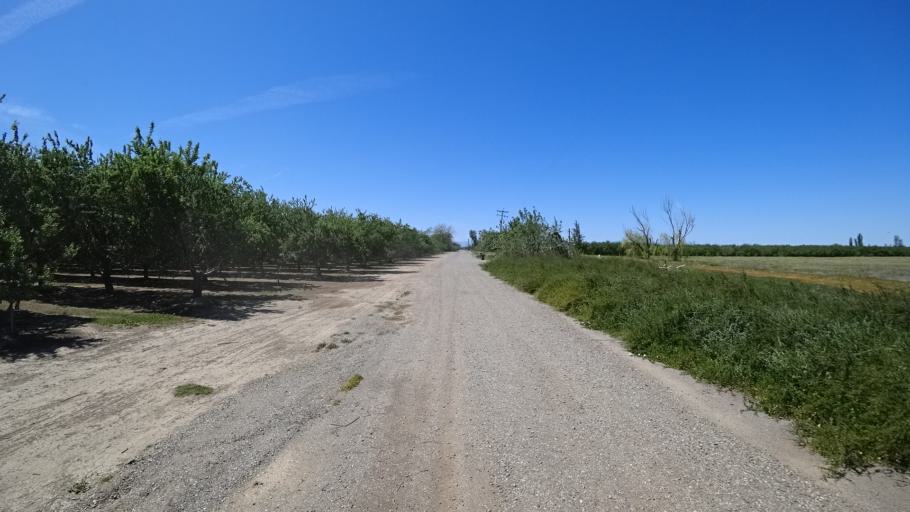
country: US
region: California
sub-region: Glenn County
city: Hamilton City
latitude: 39.7216
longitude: -122.0856
